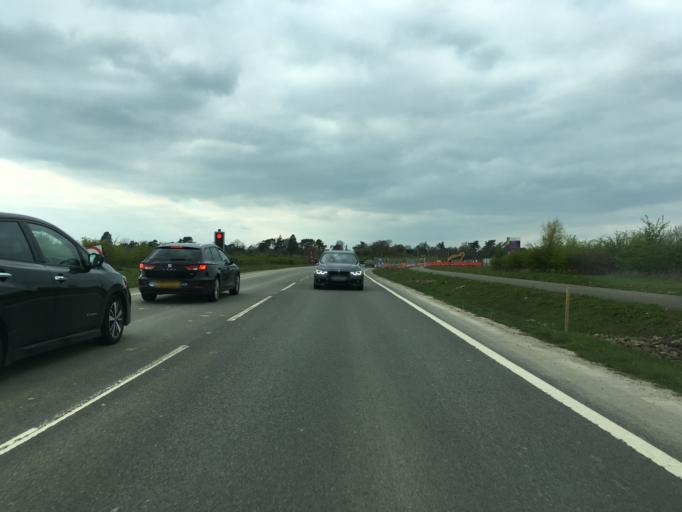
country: GB
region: England
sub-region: Oxfordshire
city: Bicester
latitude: 51.8935
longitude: -1.1800
